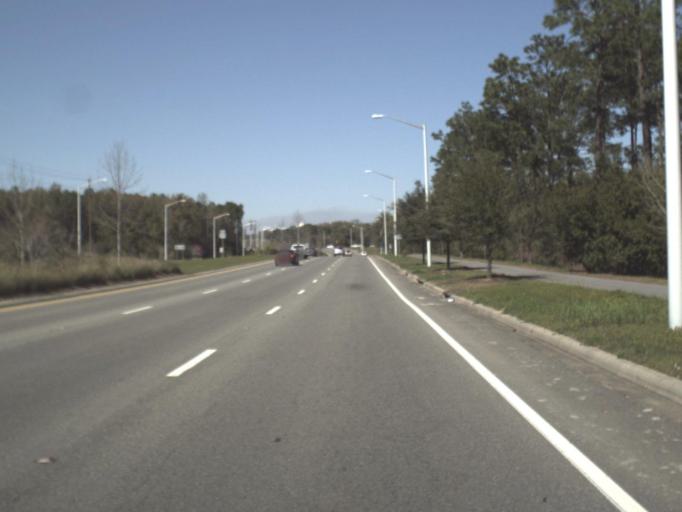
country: US
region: Florida
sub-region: Leon County
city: Woodville
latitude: 30.3824
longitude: -84.2363
